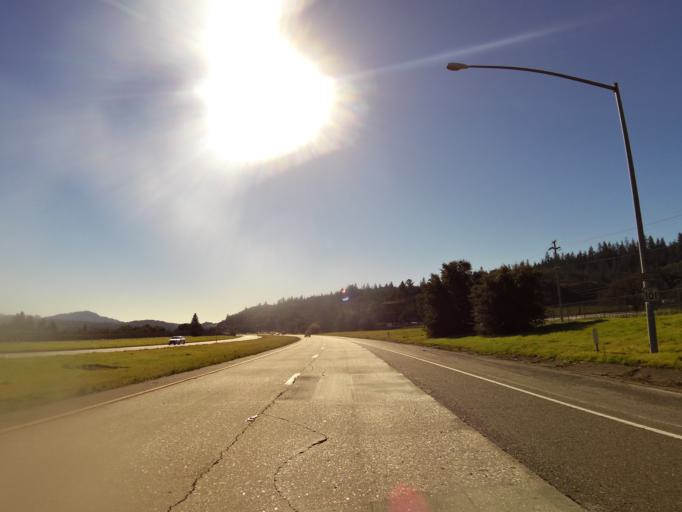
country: US
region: California
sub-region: Sonoma County
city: Healdsburg
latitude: 38.6764
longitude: -122.8808
